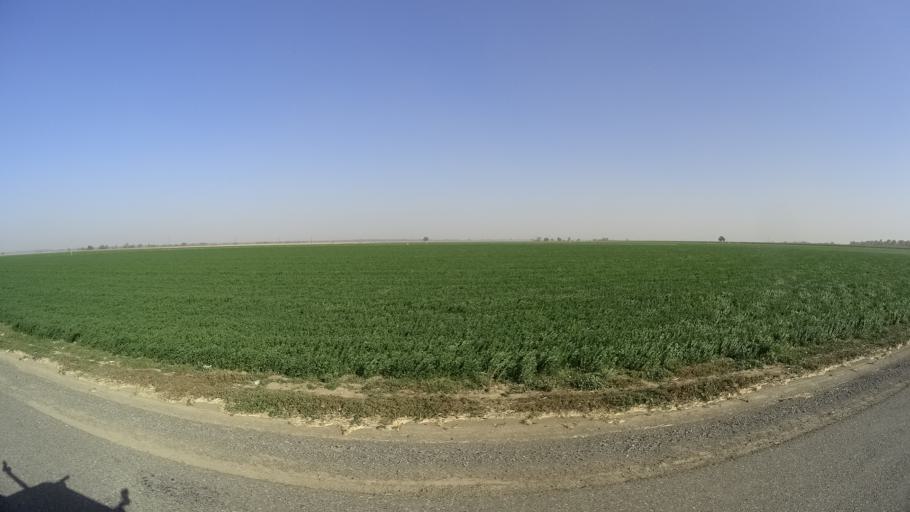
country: US
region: California
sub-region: Yolo County
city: Woodland
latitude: 38.7396
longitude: -121.7295
